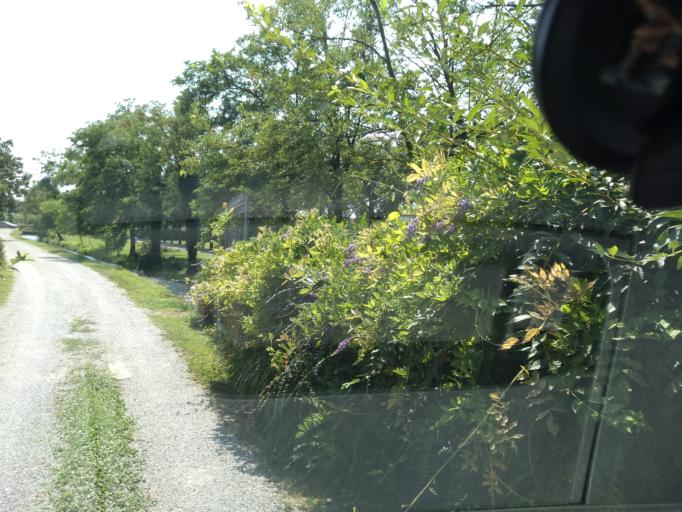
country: IT
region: Lombardy
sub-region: Provincia di Bergamo
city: Geromina
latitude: 45.5242
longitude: 9.5686
